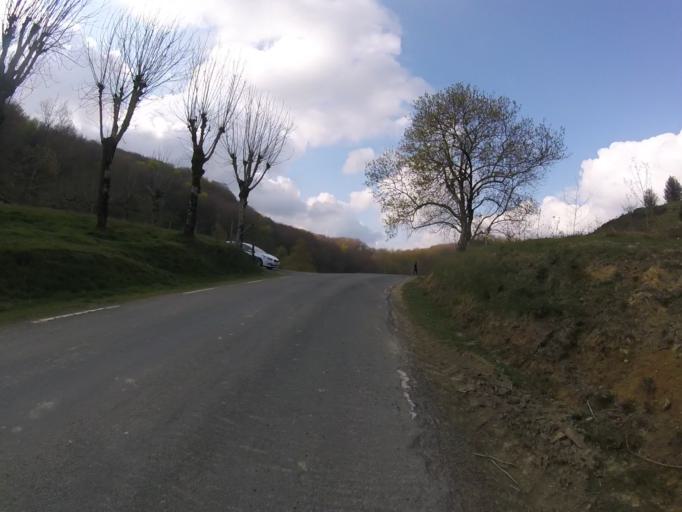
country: ES
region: Basque Country
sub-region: Provincia de Guipuzcoa
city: Azkoitia
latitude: 43.2091
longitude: -2.3215
